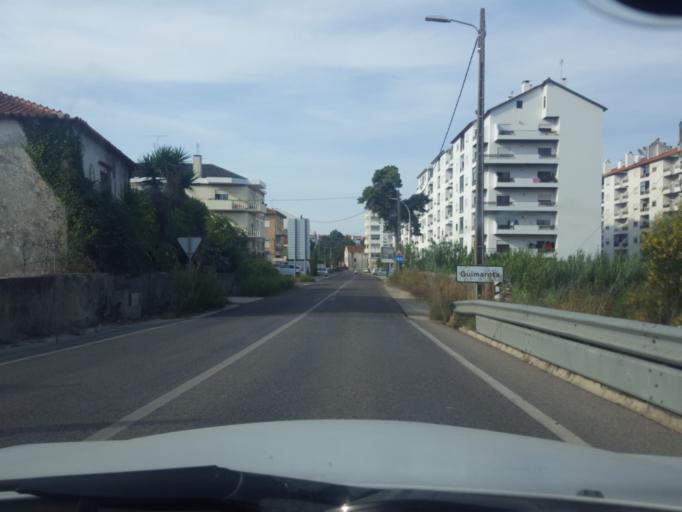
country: PT
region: Leiria
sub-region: Leiria
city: Leiria
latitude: 39.7286
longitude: -8.7978
